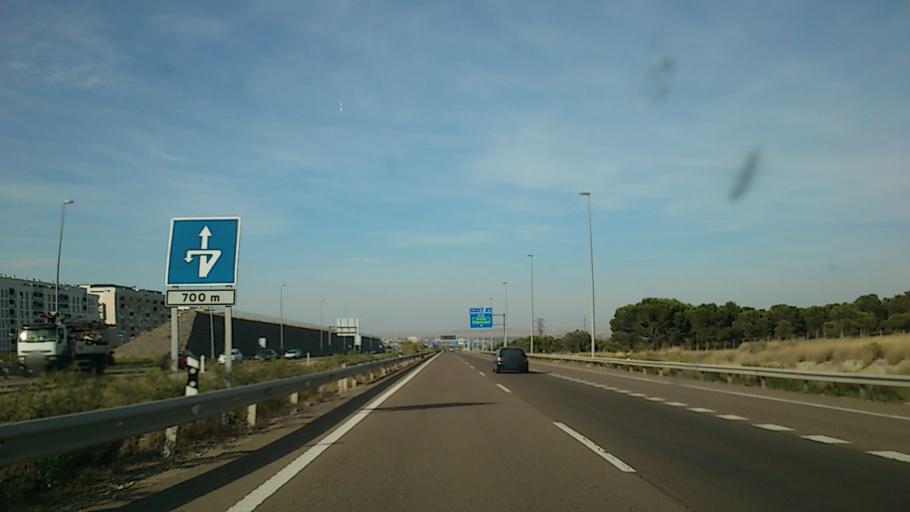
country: ES
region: Aragon
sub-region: Provincia de Zaragoza
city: Zaragoza
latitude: 41.6124
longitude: -0.8723
